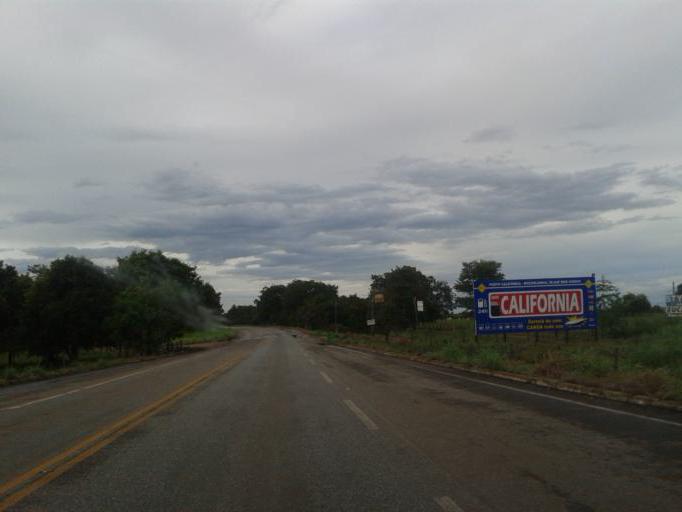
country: BR
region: Goias
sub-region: Mozarlandia
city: Mozarlandia
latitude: -14.8047
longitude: -50.5334
